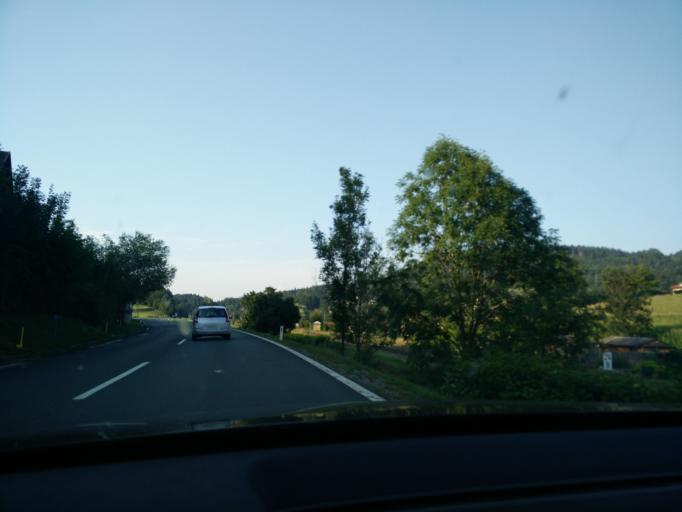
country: AT
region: Carinthia
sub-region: Politischer Bezirk Klagenfurt Land
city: Maria Rain
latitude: 46.5646
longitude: 14.2844
